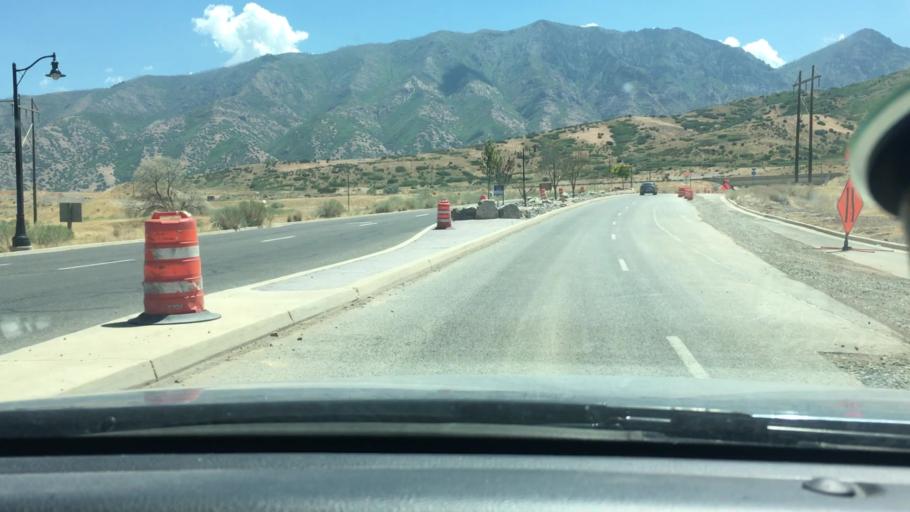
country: US
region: Utah
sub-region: Utah County
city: Santaquin
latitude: 39.9519
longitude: -111.8062
